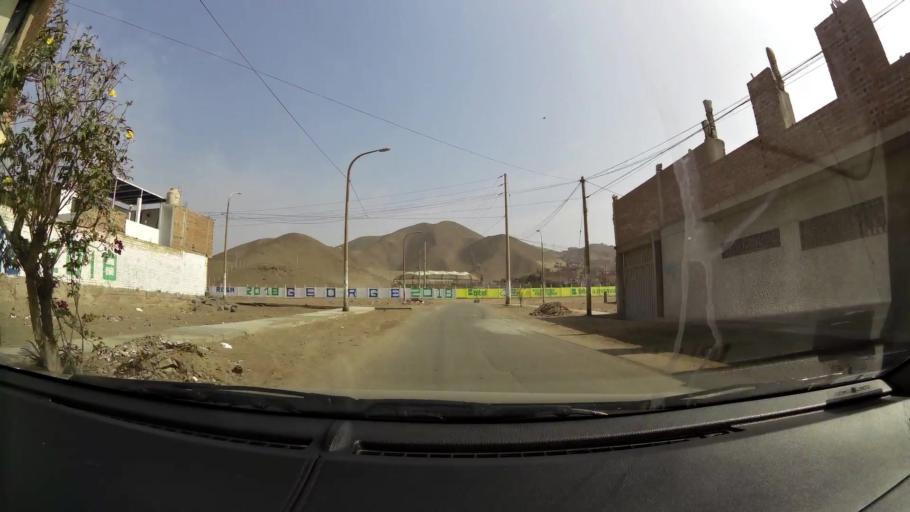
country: PE
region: Lima
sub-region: Lima
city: Santa Rosa
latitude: -11.7852
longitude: -77.1582
